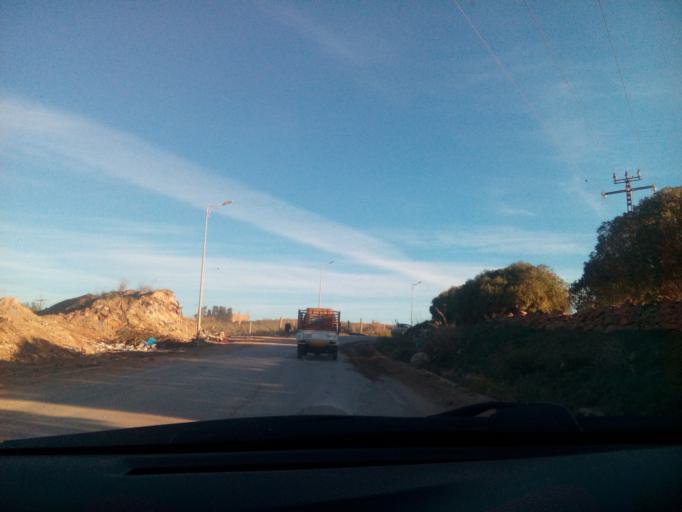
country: DZ
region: Oran
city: Es Senia
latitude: 35.6265
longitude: -0.6778
